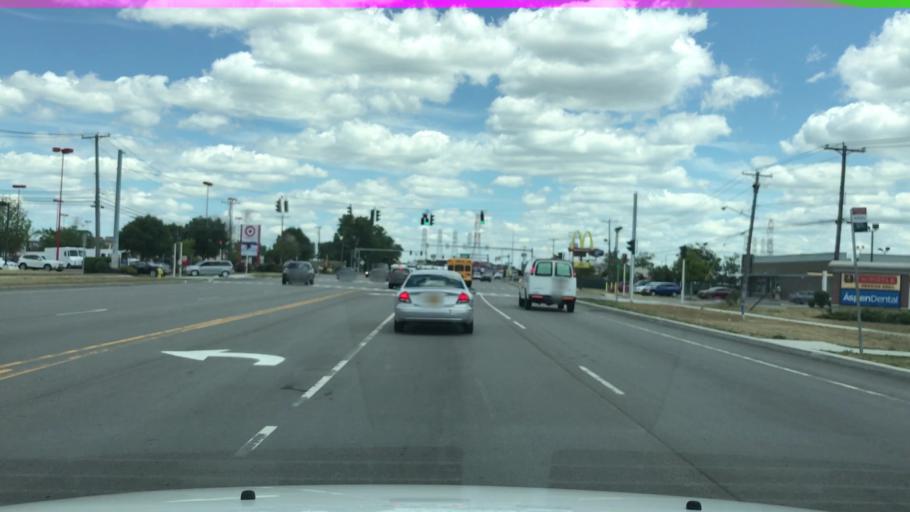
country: US
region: New York
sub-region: Erie County
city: Cheektowaga
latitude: 42.9080
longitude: -78.7744
